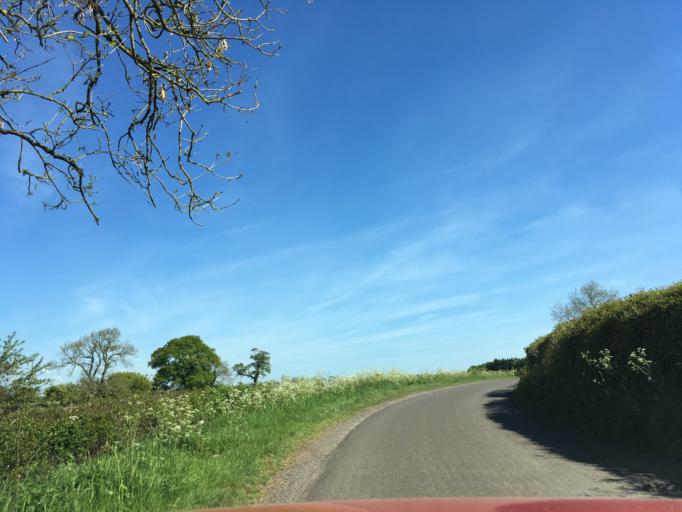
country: GB
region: England
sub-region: Wiltshire
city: Luckington
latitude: 51.5833
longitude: -2.2511
